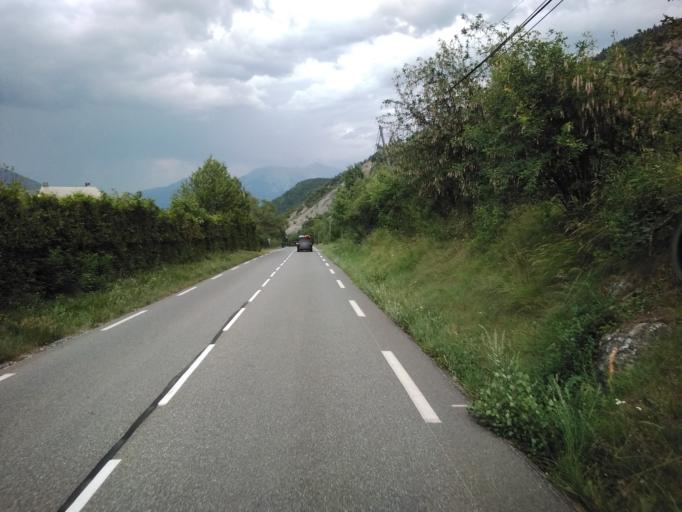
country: FR
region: Provence-Alpes-Cote d'Azur
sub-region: Departement des Hautes-Alpes
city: Chorges
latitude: 44.5140
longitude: 6.3734
